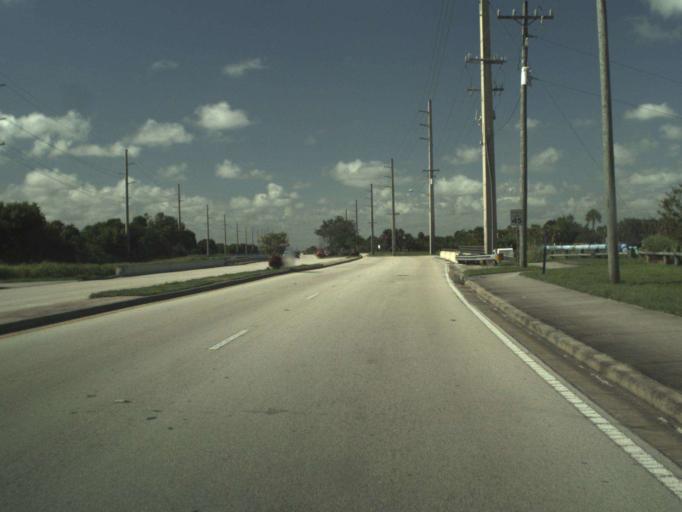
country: US
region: Florida
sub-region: Indian River County
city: Vero Beach South
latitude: 27.6348
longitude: -80.4468
